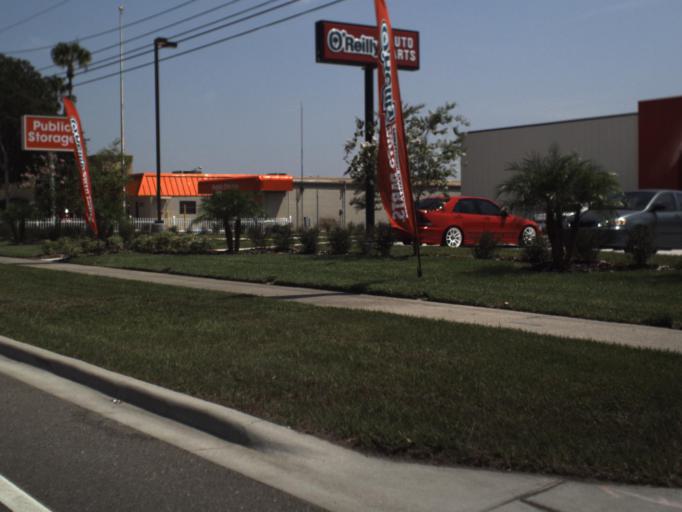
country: US
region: Florida
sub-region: Hillsborough County
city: Egypt Lake-Leto
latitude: 28.0204
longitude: -82.5049
